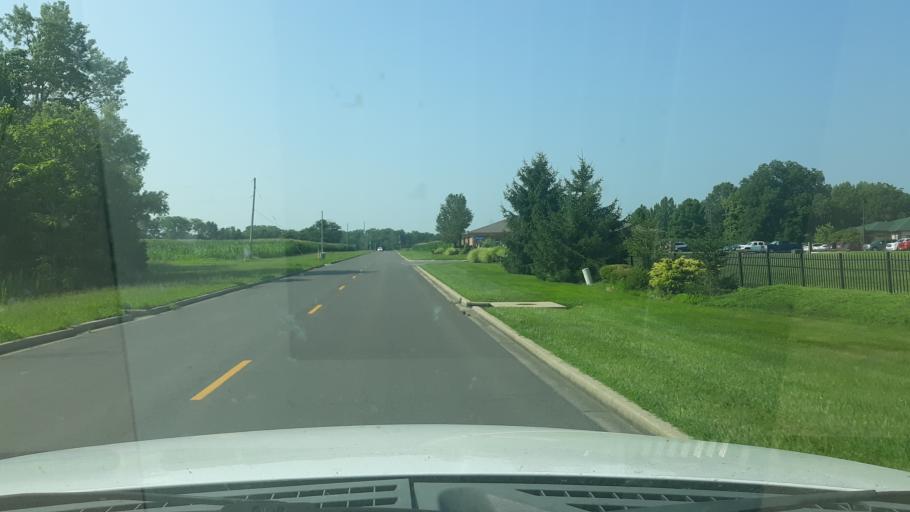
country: US
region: Illinois
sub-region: Williamson County
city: Energy
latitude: 37.7370
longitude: -88.9932
